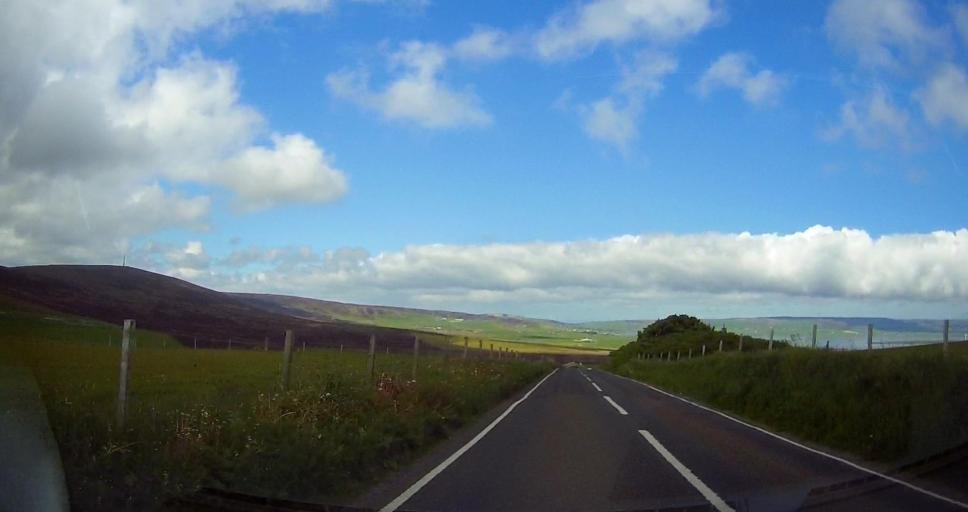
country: GB
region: Scotland
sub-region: Orkney Islands
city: Orkney
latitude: 58.9808
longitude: -3.0374
